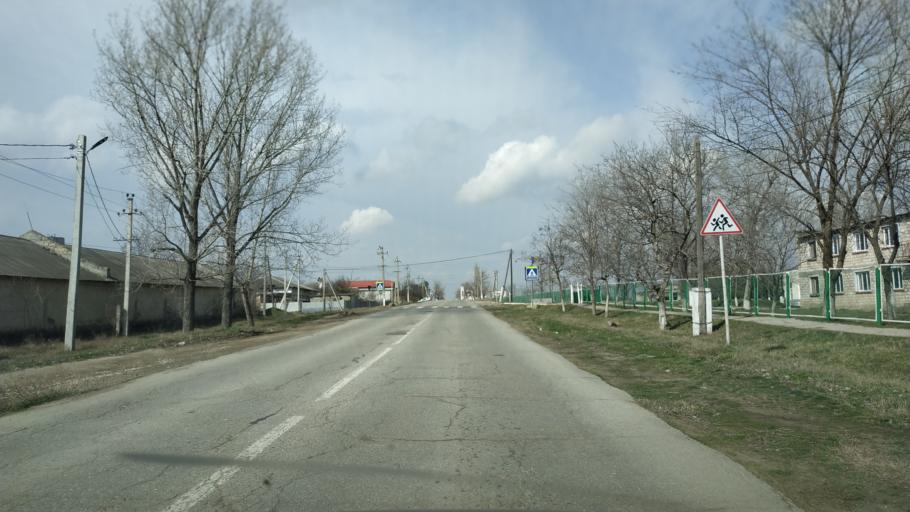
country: MD
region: Gagauzia
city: Vulcanesti
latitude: 45.6952
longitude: 28.4043
